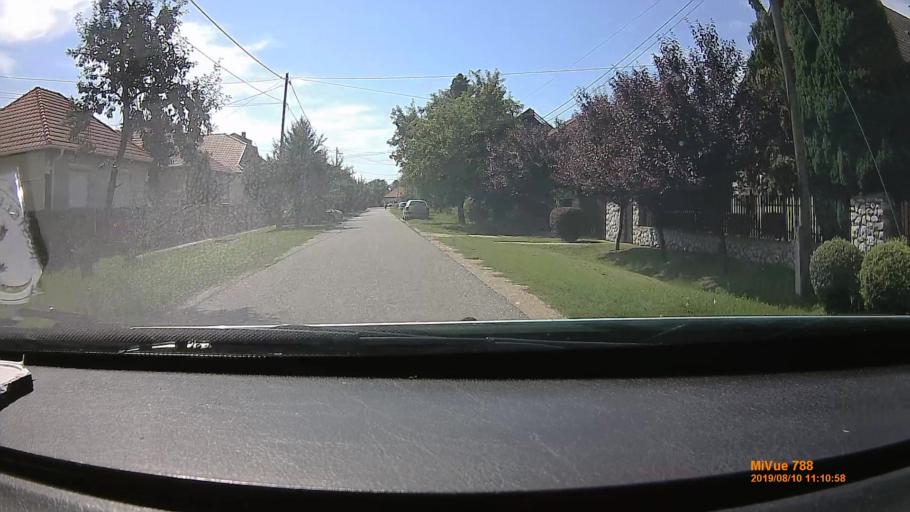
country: HU
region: Borsod-Abauj-Zemplen
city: Emod
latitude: 47.9326
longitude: 20.8108
